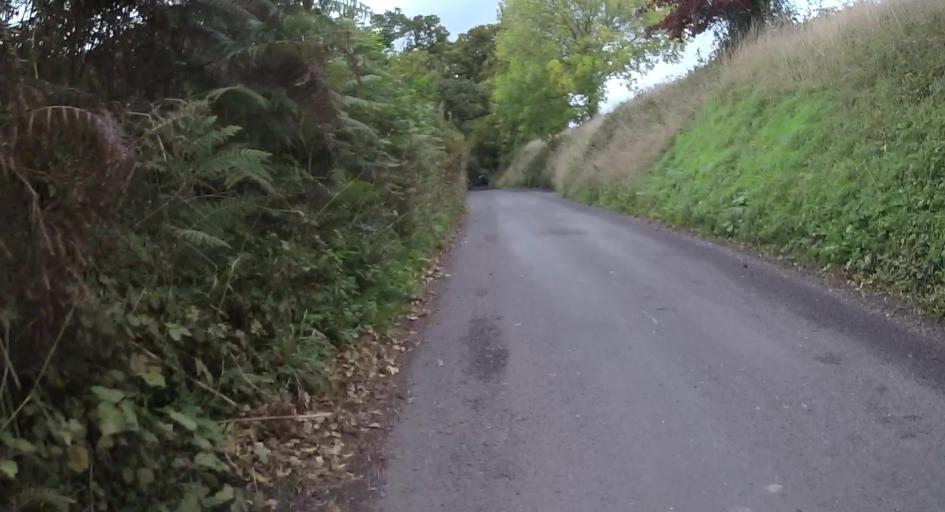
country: GB
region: England
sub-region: Hampshire
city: Alton
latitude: 51.1344
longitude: -0.9356
